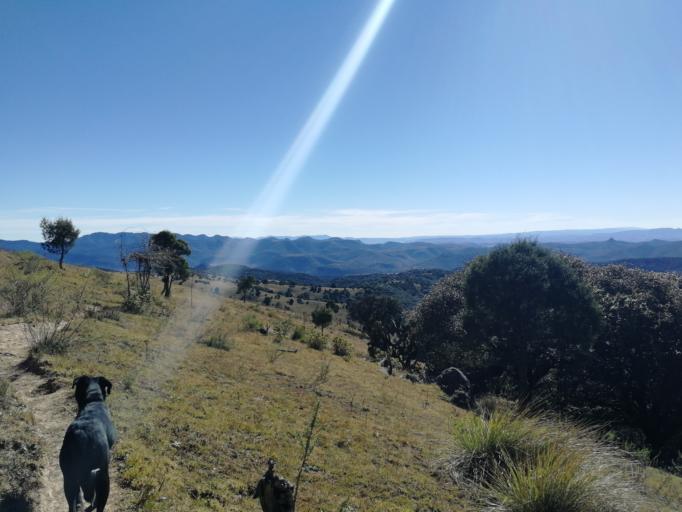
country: MX
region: San Luis Potosi
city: Zaragoza
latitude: 22.0064
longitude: -100.6142
